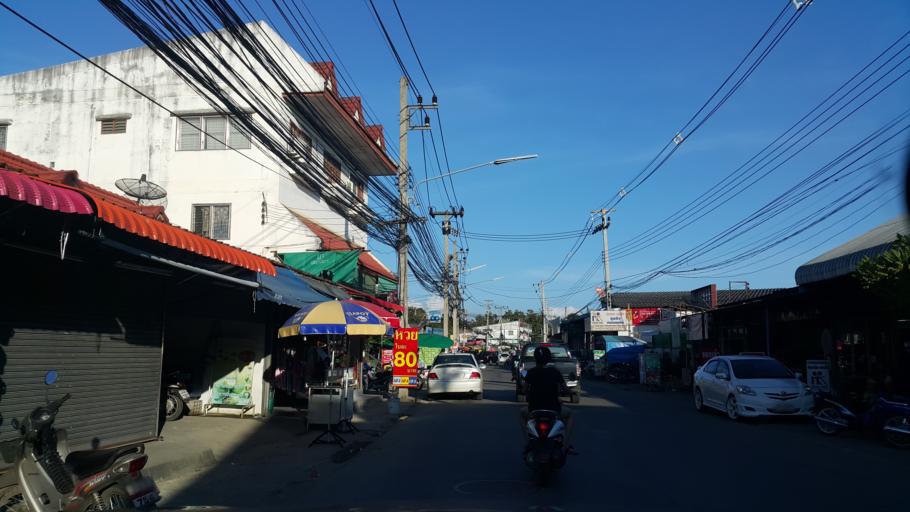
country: TH
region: Lamphun
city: Lamphun
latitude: 18.5994
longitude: 99.0271
